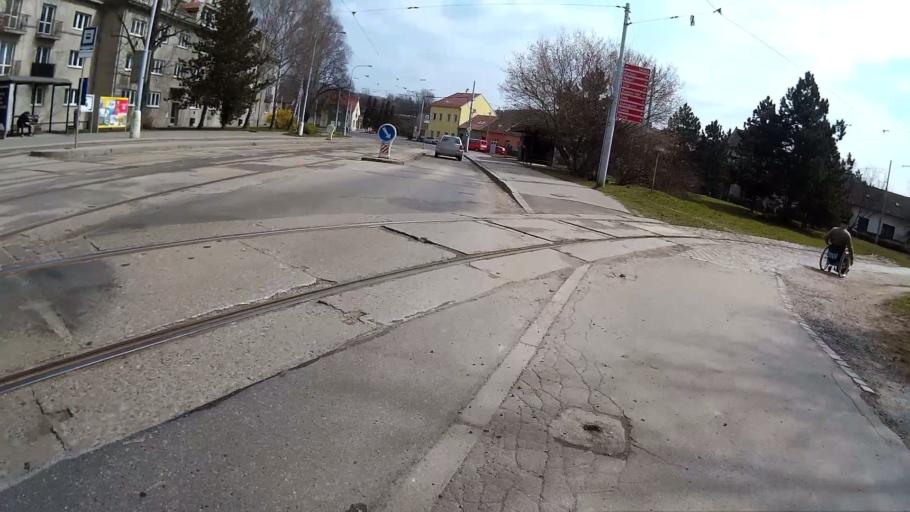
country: CZ
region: South Moravian
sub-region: Mesto Brno
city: Brno
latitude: 49.2156
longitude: 16.6424
